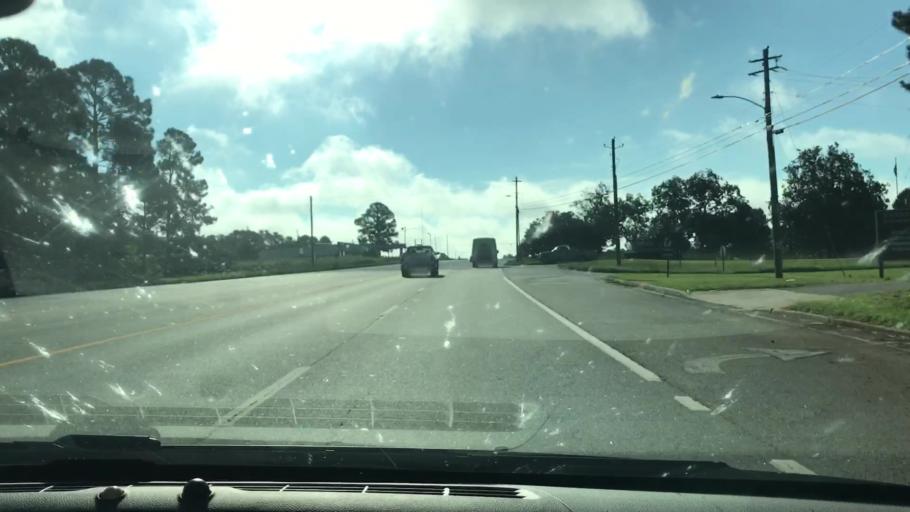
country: US
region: Georgia
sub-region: Terrell County
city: Dawson
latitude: 31.7611
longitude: -84.4362
